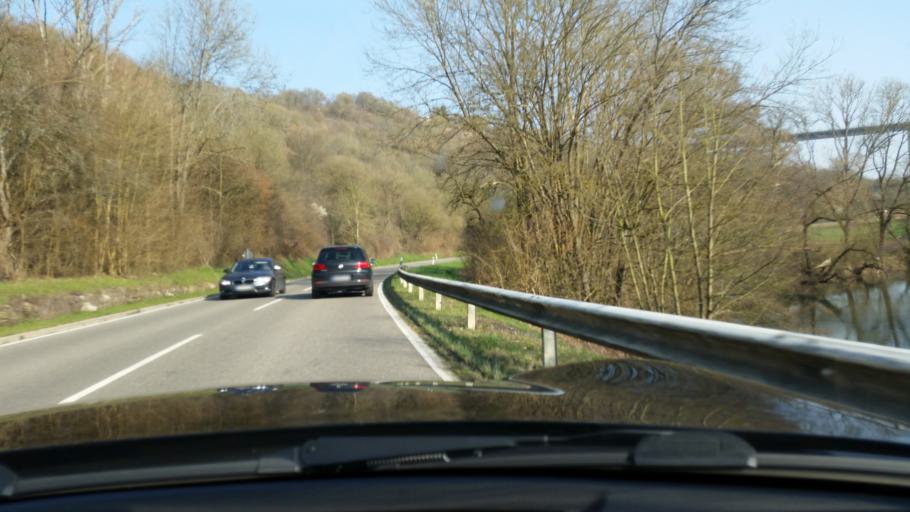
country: DE
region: Baden-Wuerttemberg
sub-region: Regierungsbezirk Stuttgart
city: Widdern
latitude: 49.3232
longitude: 9.4042
